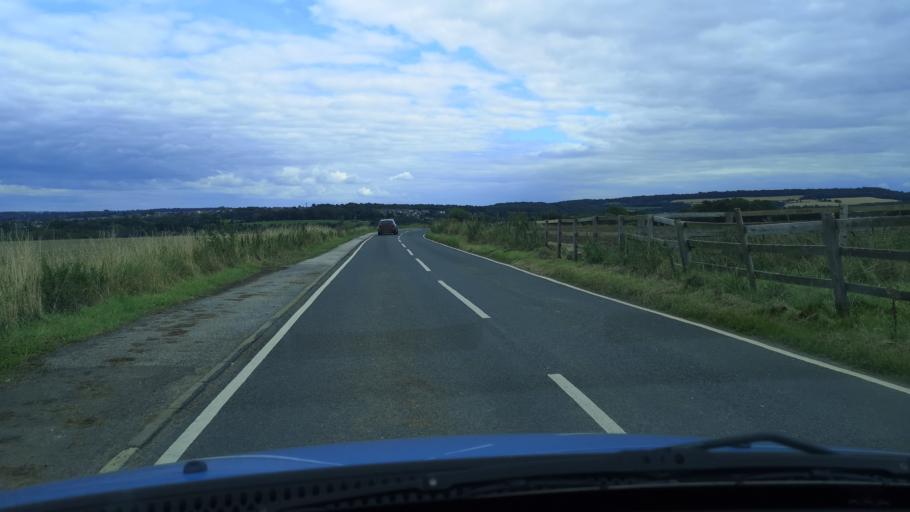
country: GB
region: England
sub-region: City and Borough of Wakefield
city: Horbury
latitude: 53.6471
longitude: -1.5621
